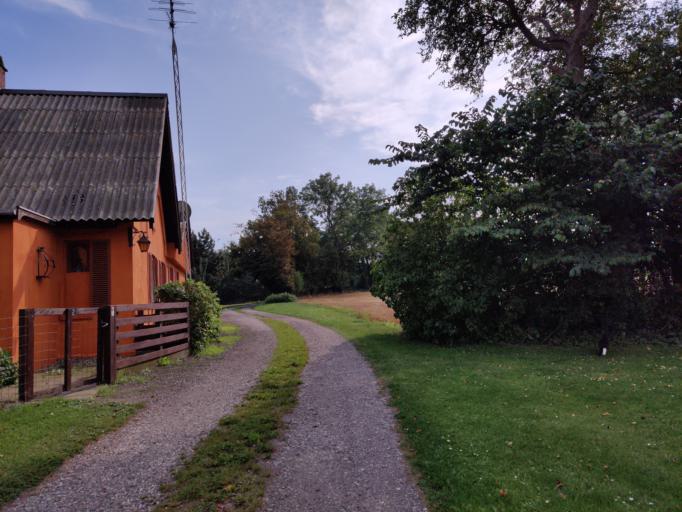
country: DK
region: Zealand
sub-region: Guldborgsund Kommune
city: Nykobing Falster
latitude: 54.7011
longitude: 11.9038
